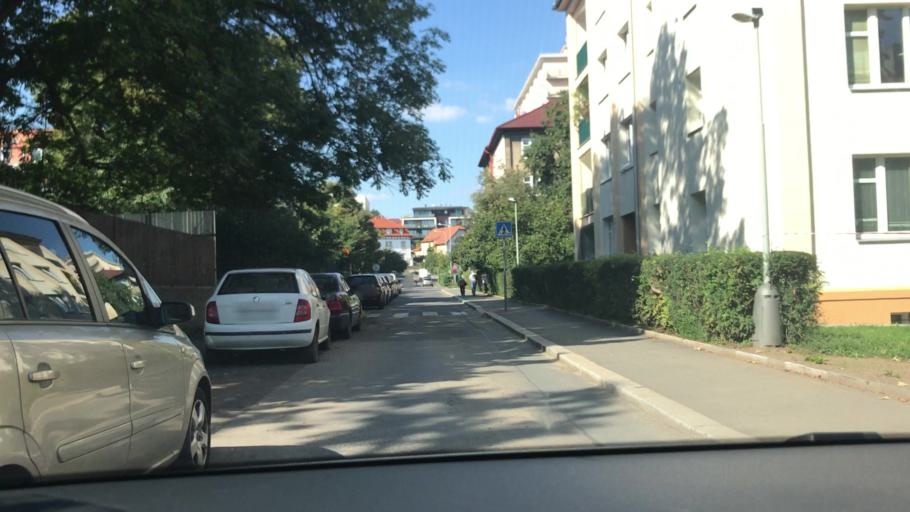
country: CZ
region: Praha
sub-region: Praha 8
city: Liben
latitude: 50.0749
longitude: 14.4936
